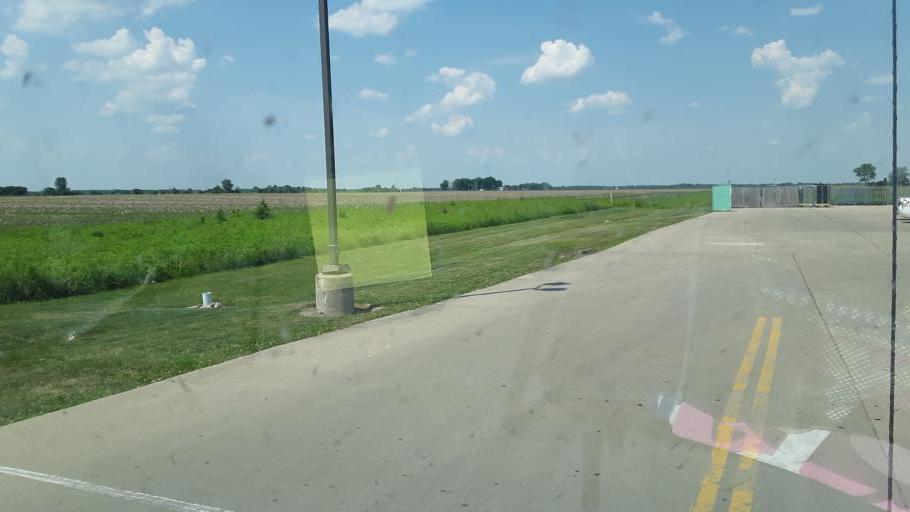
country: US
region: Illinois
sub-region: Vermilion County
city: Oakwood
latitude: 40.1221
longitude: -87.7784
